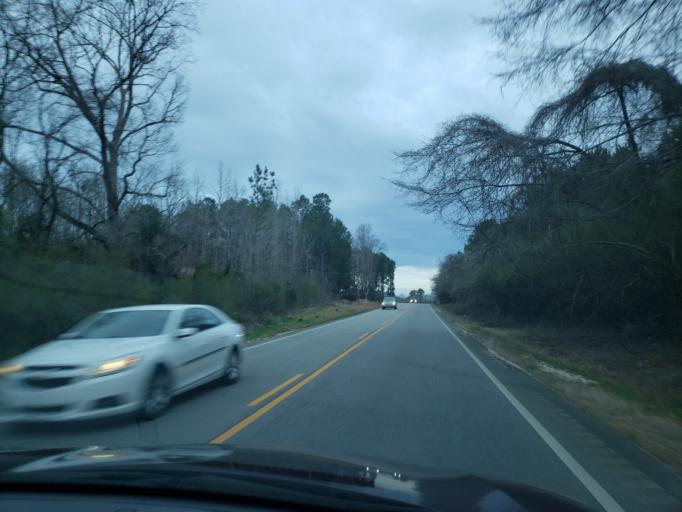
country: US
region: Alabama
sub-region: Chambers County
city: Lafayette
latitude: 32.9821
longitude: -85.4030
